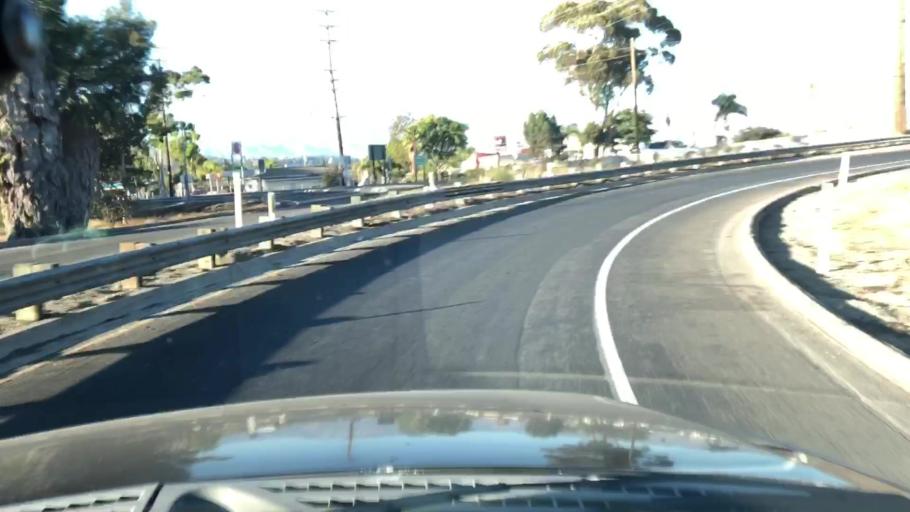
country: US
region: California
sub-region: Ventura County
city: Saticoy
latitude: 34.2900
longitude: -119.1578
